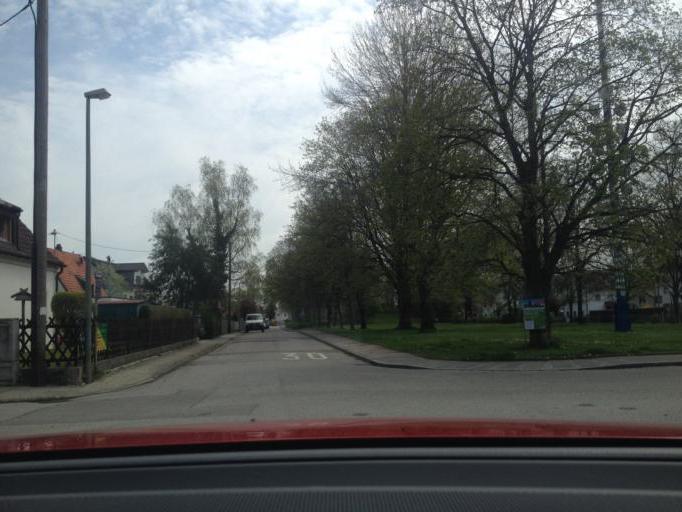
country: DE
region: Bavaria
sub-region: Upper Bavaria
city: Vaterstetten
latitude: 48.0961
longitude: 11.7621
